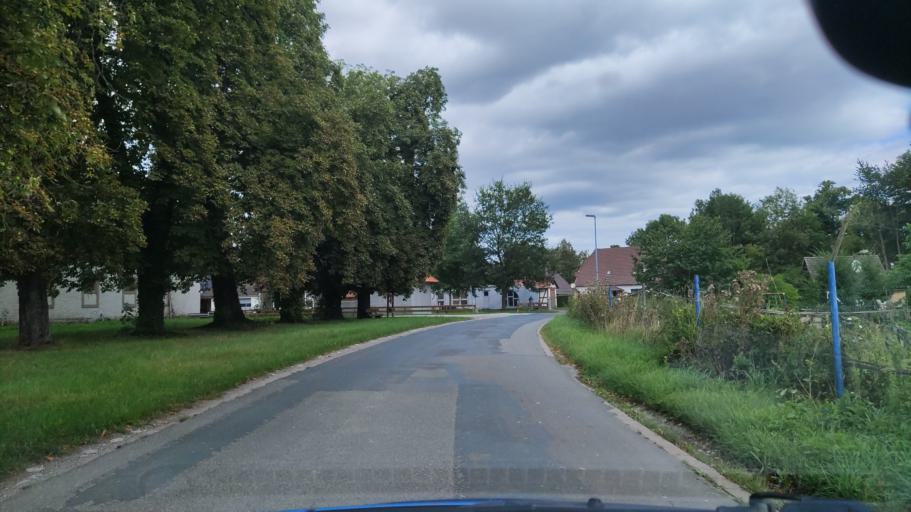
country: DE
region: Lower Saxony
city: Dassel
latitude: 51.8231
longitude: 9.7165
